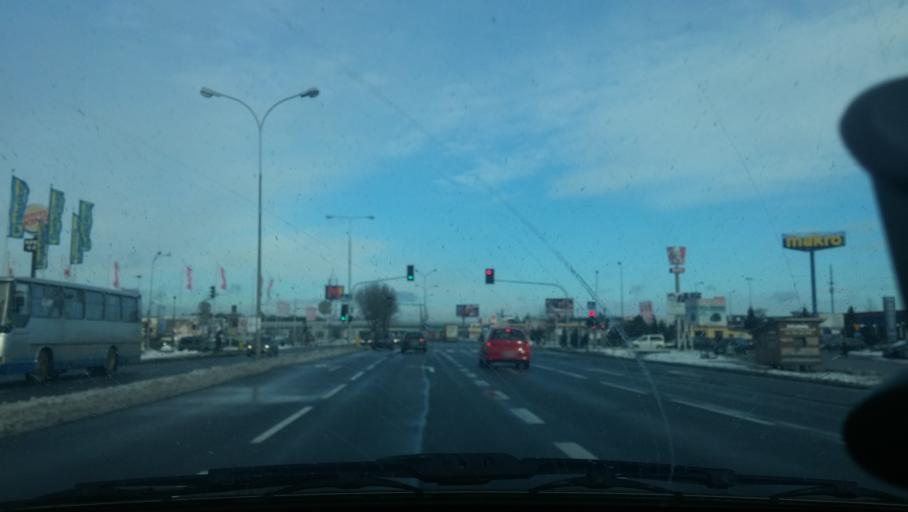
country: PL
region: Masovian Voivodeship
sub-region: Powiat wolominski
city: Zabki
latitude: 52.3026
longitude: 21.0883
